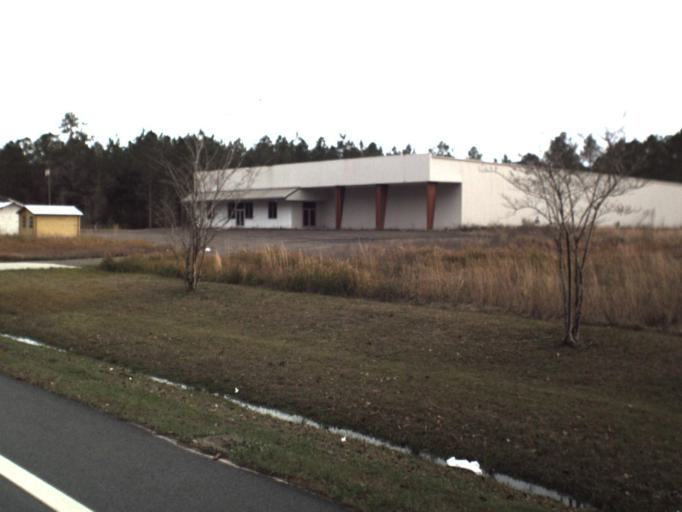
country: US
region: Florida
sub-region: Gulf County
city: Wewahitchka
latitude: 30.1160
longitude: -85.2064
